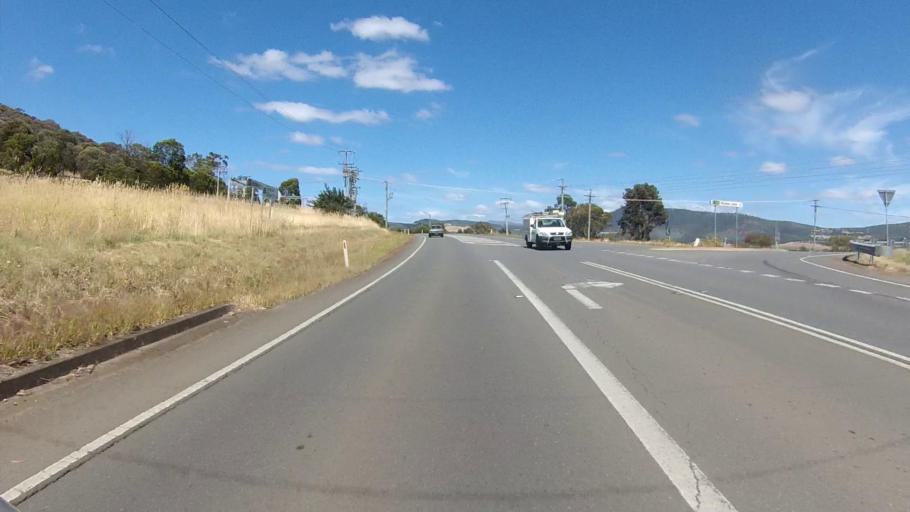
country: AU
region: Tasmania
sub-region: Clarence
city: Cambridge
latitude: -42.7427
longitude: 147.4204
